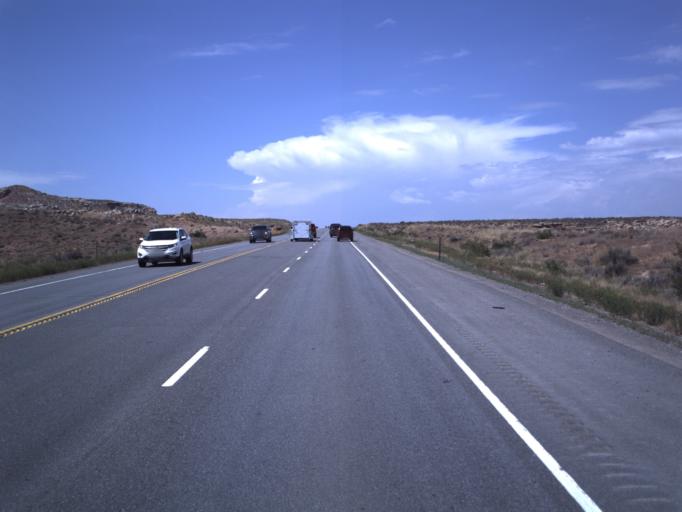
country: US
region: Utah
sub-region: Uintah County
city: Maeser
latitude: 40.3133
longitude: -109.7097
